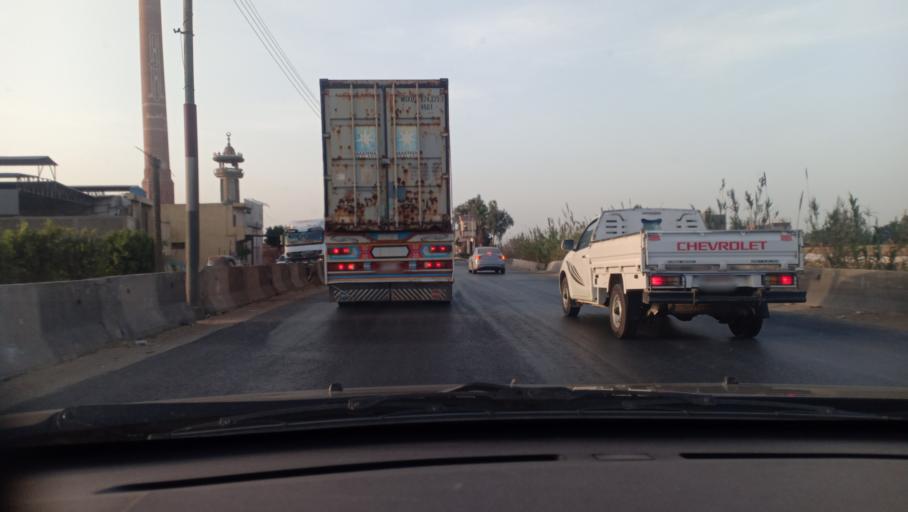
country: EG
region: Muhafazat al Gharbiyah
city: Zifta
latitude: 30.6057
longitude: 31.2751
